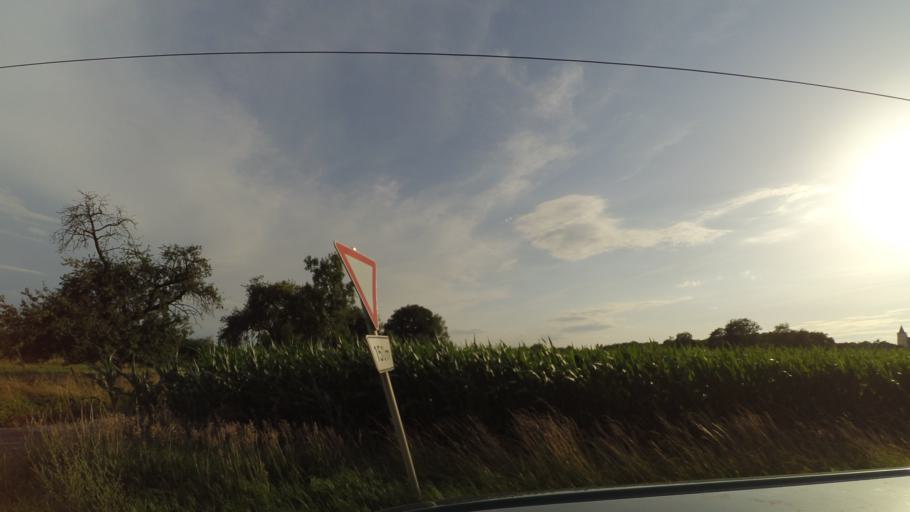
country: DE
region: Bavaria
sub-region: Swabia
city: Lauingen
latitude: 48.5647
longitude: 10.4420
